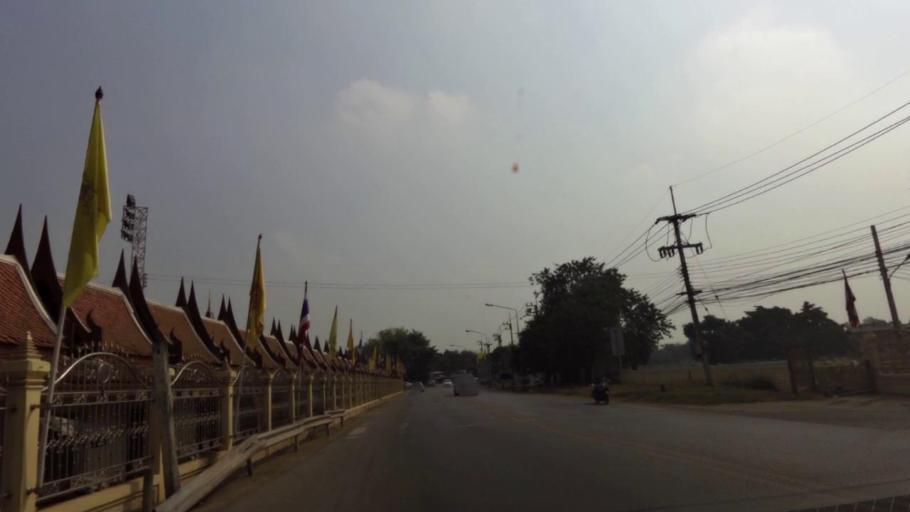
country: TH
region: Phra Nakhon Si Ayutthaya
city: Phra Nakhon Si Ayutthaya
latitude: 14.3433
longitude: 100.5792
